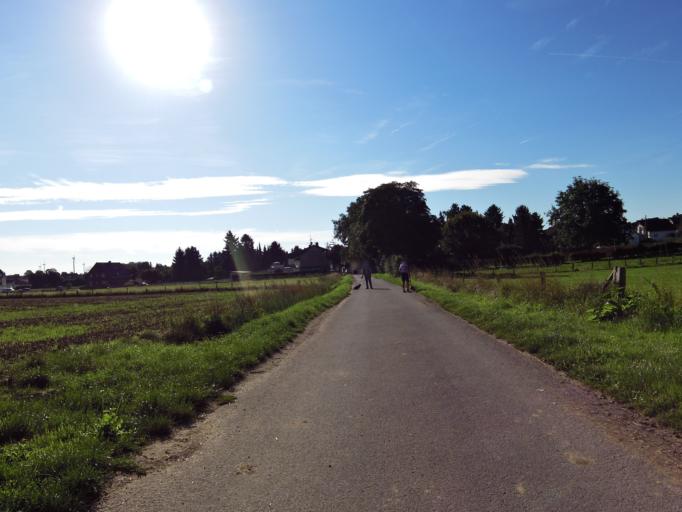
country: DE
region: North Rhine-Westphalia
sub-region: Regierungsbezirk Koln
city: Alsdorf
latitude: 50.8713
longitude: 6.1993
